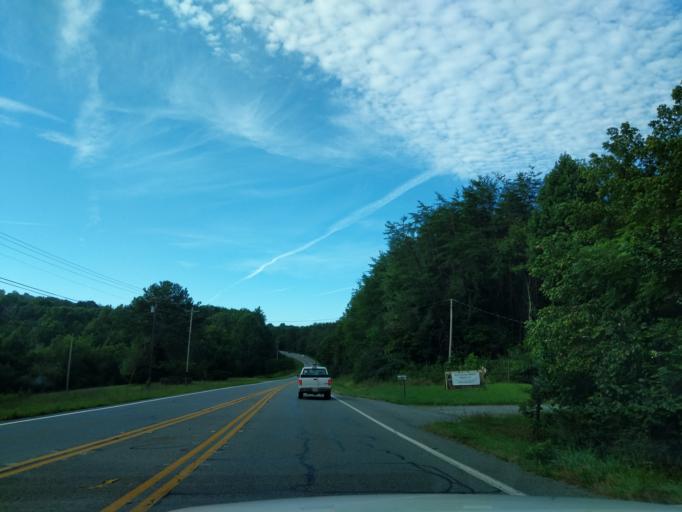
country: US
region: Georgia
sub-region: Fannin County
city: McCaysville
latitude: 34.9441
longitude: -84.3755
